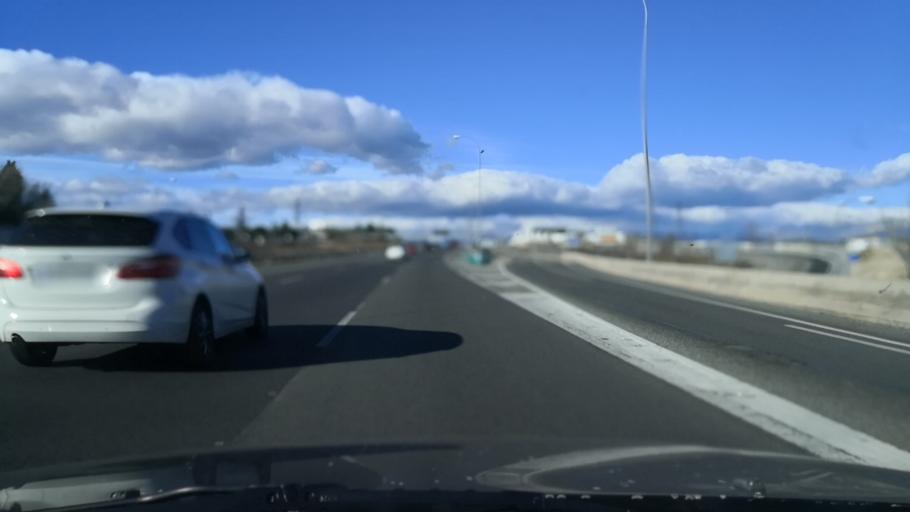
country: ES
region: Madrid
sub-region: Provincia de Madrid
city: Las Rozas de Madrid
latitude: 40.4992
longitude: -3.8723
